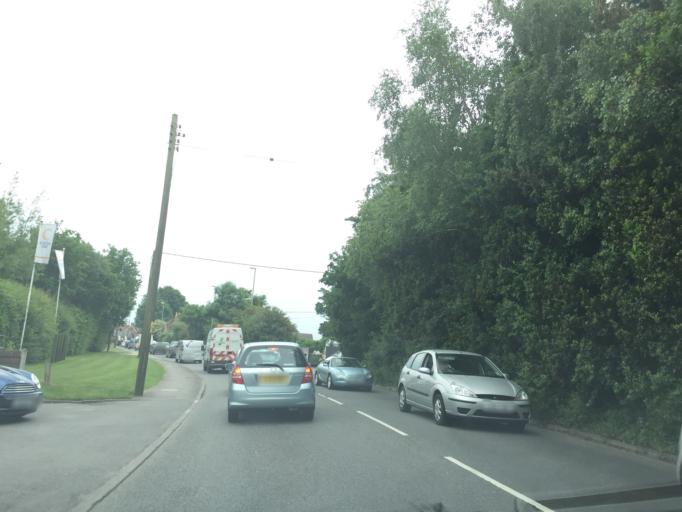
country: GB
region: England
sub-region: Dorset
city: Ferndown
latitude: 50.7844
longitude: -1.9079
